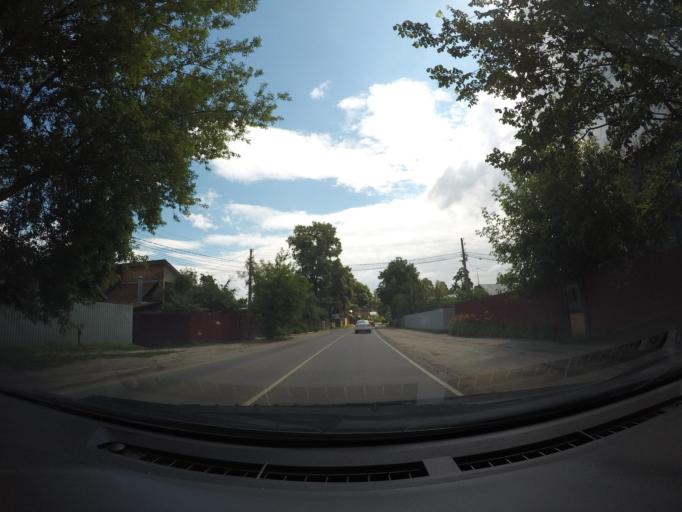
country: RU
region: Moskovskaya
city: Kraskovo
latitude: 55.6567
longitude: 37.9878
